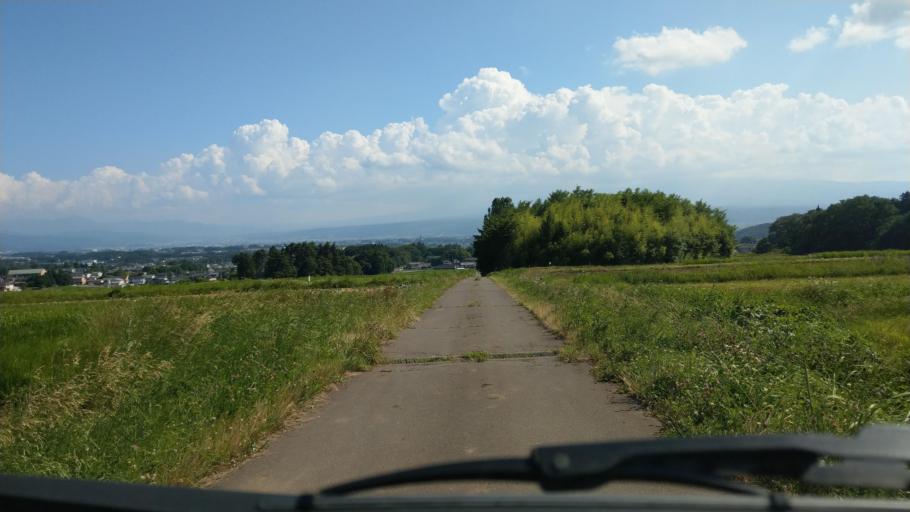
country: JP
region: Nagano
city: Komoro
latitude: 36.3281
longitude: 138.4506
